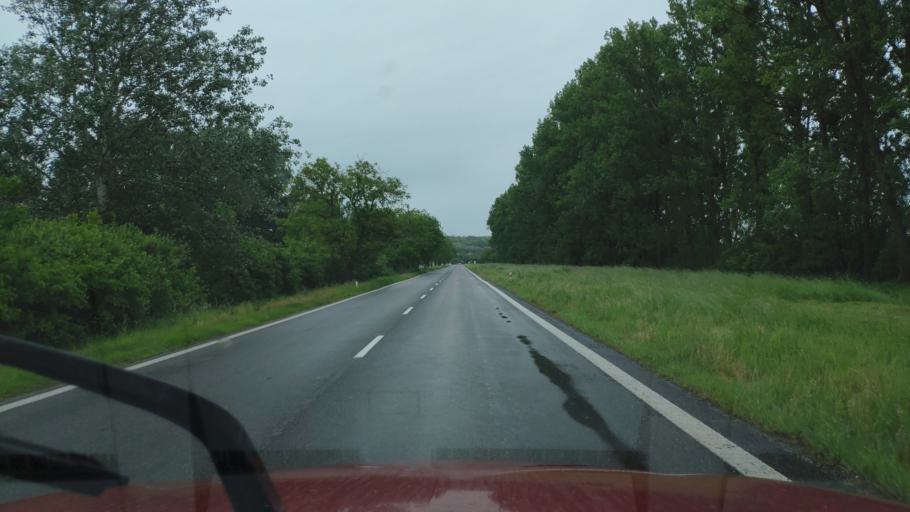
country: HU
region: Borsod-Abauj-Zemplen
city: Ricse
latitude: 48.4322
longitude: 21.9072
